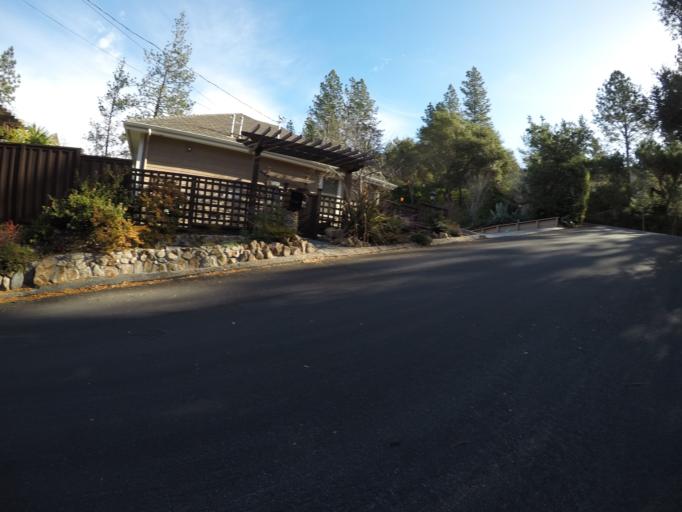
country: US
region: California
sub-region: Santa Cruz County
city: Mount Hermon
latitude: 37.0380
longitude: -122.0371
